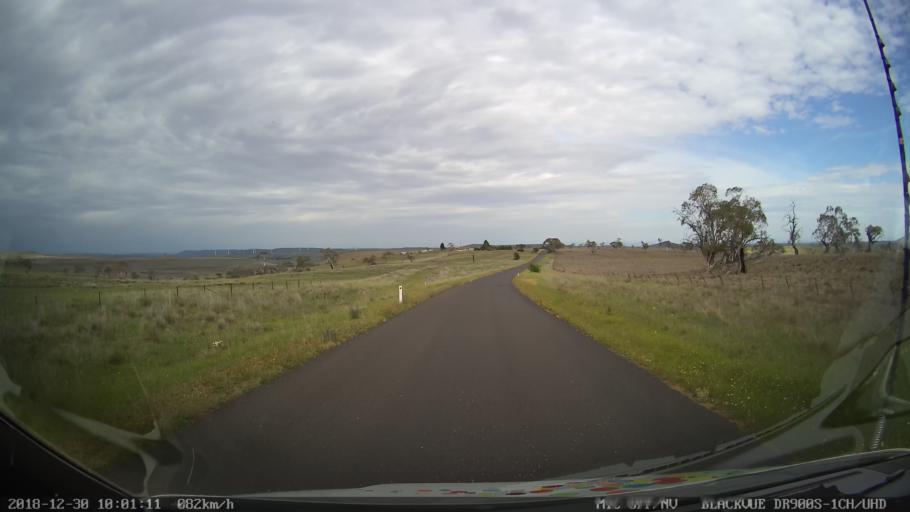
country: AU
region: New South Wales
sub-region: Cooma-Monaro
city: Cooma
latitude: -36.5143
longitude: 149.1895
